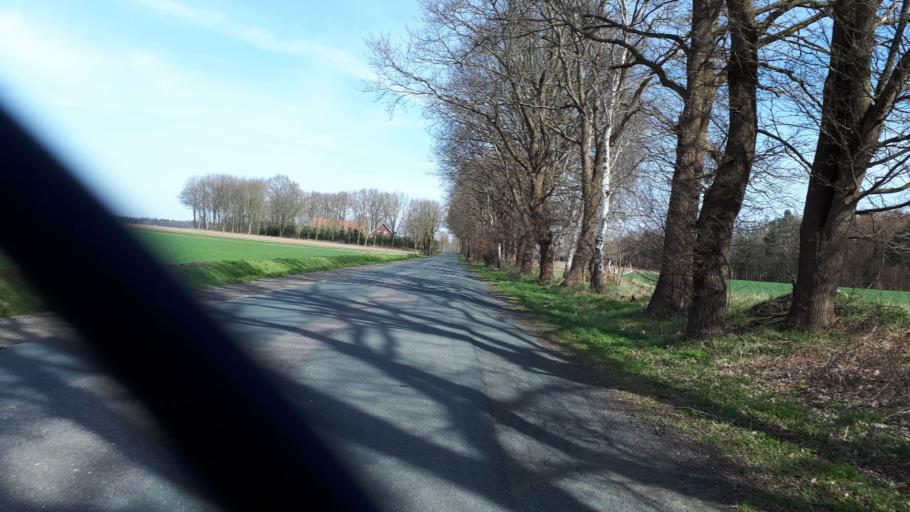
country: DE
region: Lower Saxony
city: Cloppenburg
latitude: 52.8729
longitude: 7.9984
